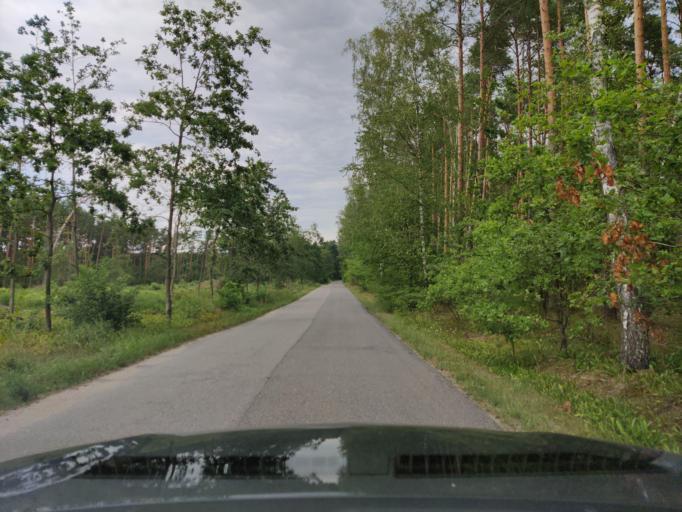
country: PL
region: Masovian Voivodeship
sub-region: Powiat pultuski
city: Pultusk
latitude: 52.7322
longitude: 21.1373
